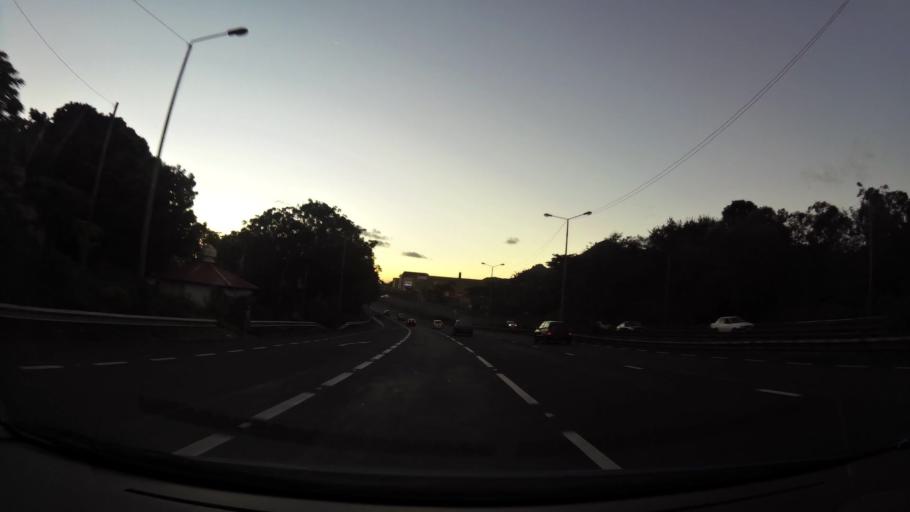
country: MU
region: Moka
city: Moka
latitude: -20.2290
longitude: 57.4999
